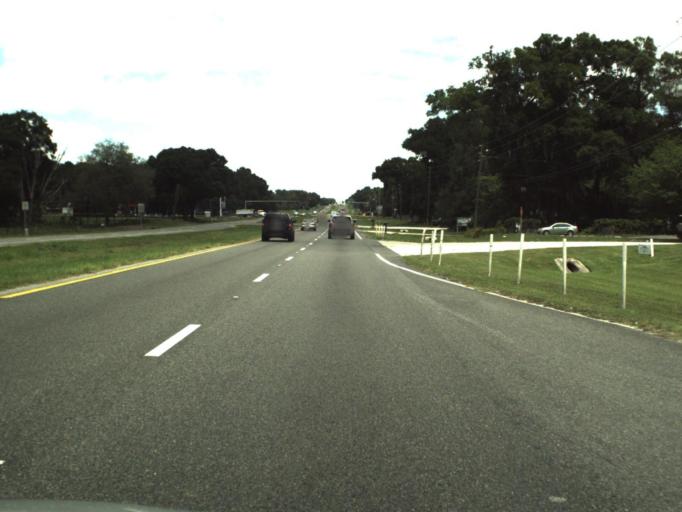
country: US
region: Florida
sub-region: Marion County
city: Ocala
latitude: 29.2626
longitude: -82.1519
